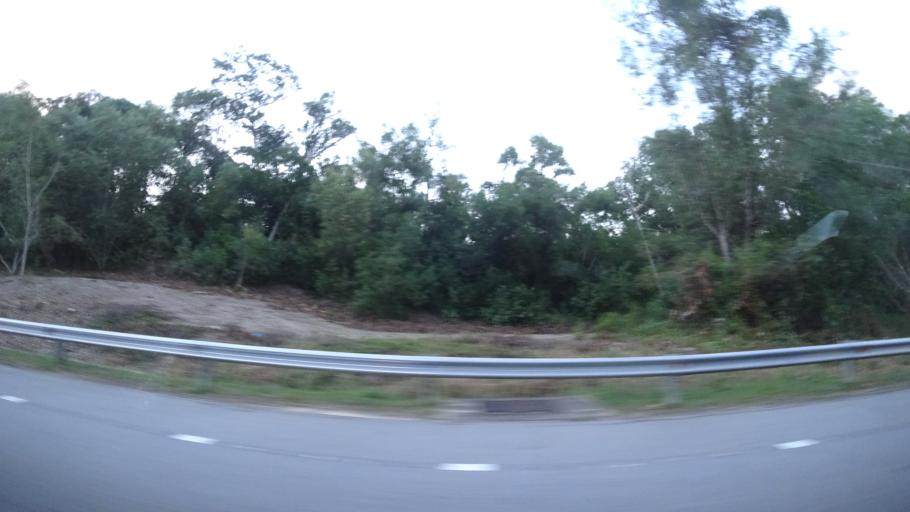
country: BN
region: Brunei and Muara
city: Bandar Seri Begawan
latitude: 4.9351
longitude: 114.8257
